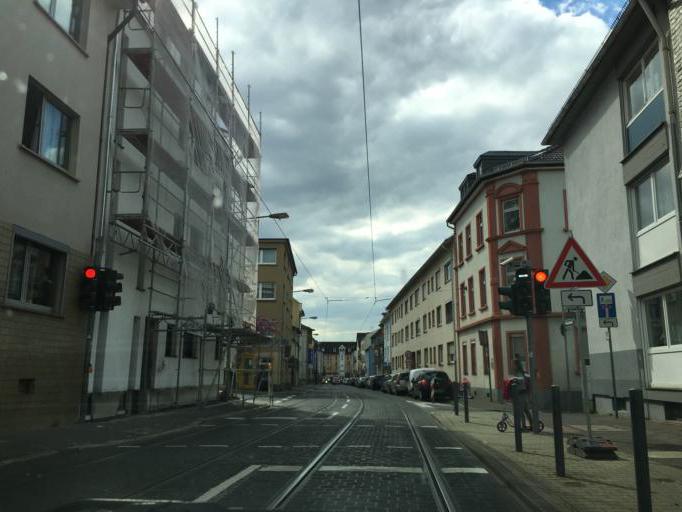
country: DE
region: Hesse
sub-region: Regierungsbezirk Darmstadt
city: Offenbach
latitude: 50.1005
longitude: 8.7278
